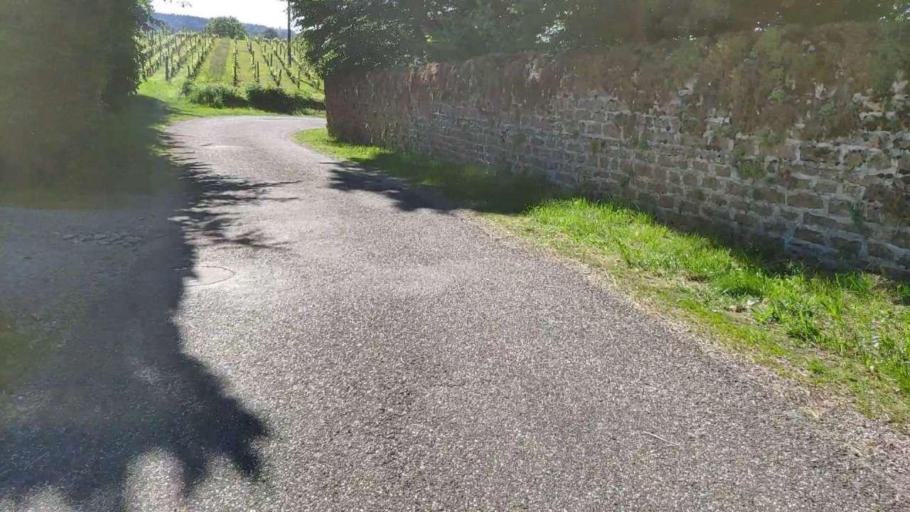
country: FR
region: Franche-Comte
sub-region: Departement du Jura
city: Perrigny
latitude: 46.7209
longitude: 5.5773
